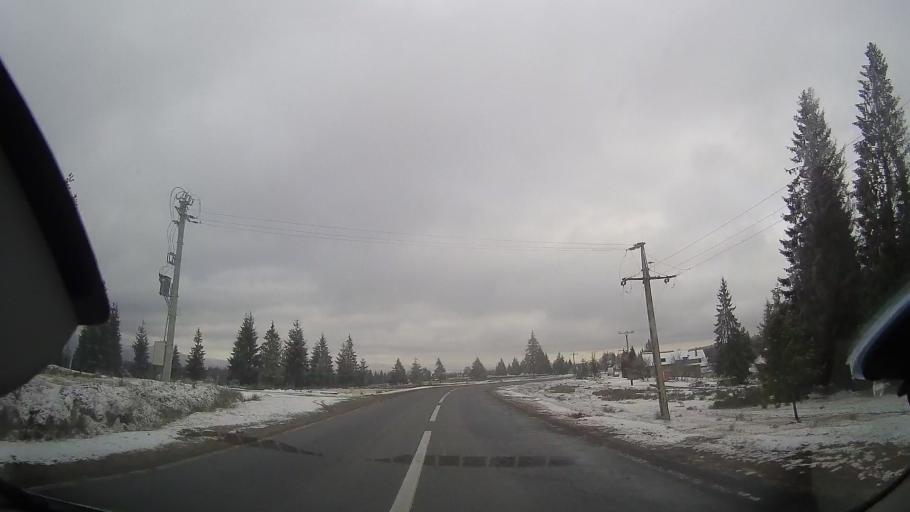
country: RO
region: Cluj
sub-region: Comuna Belis
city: Belis
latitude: 46.7008
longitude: 23.0363
